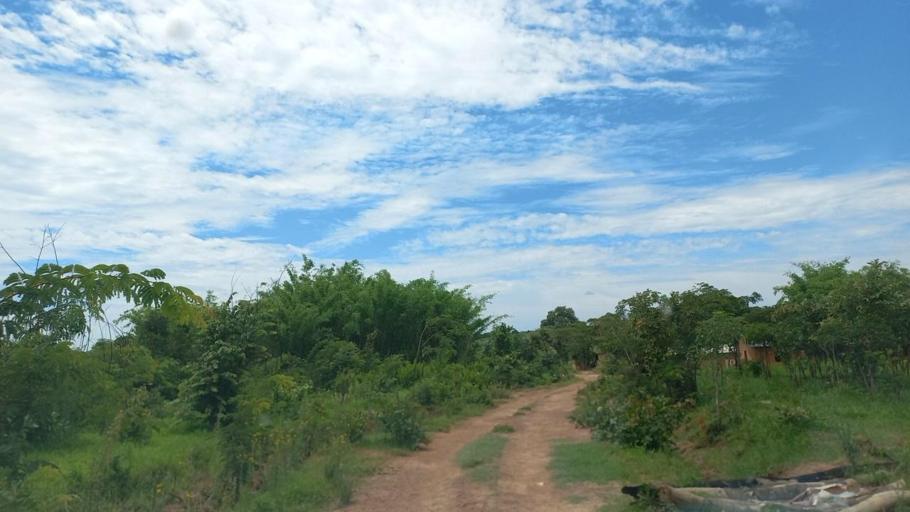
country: ZM
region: Copperbelt
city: Kitwe
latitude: -12.8154
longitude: 28.3906
